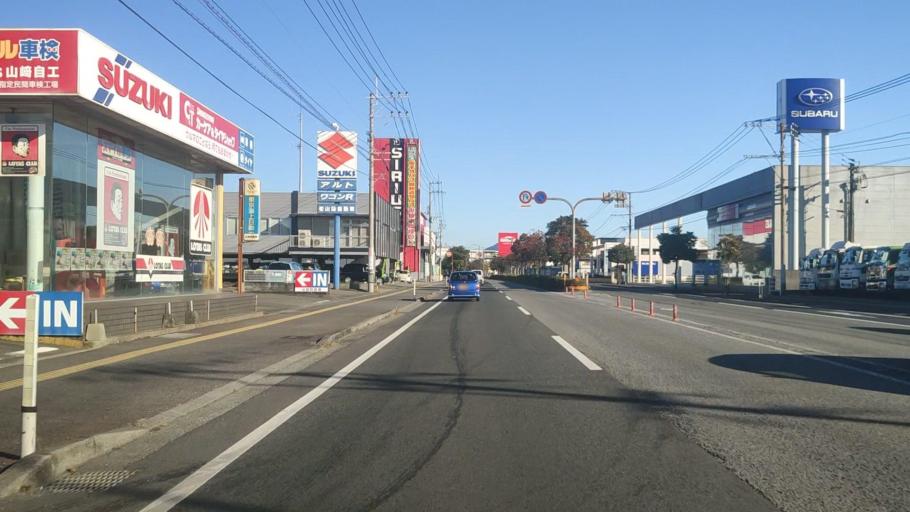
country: JP
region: Miyazaki
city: Nobeoka
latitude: 32.5664
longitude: 131.6828
